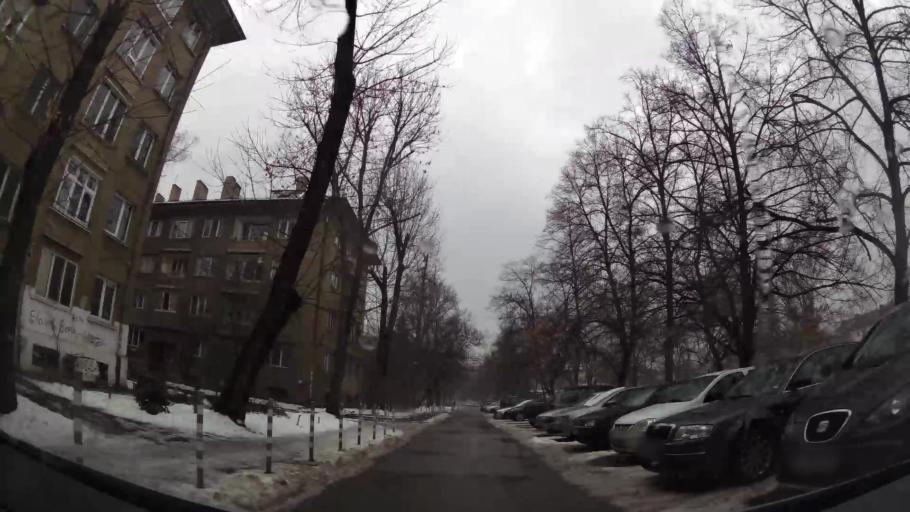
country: BG
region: Sofia-Capital
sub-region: Stolichna Obshtina
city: Sofia
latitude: 42.6761
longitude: 23.2782
